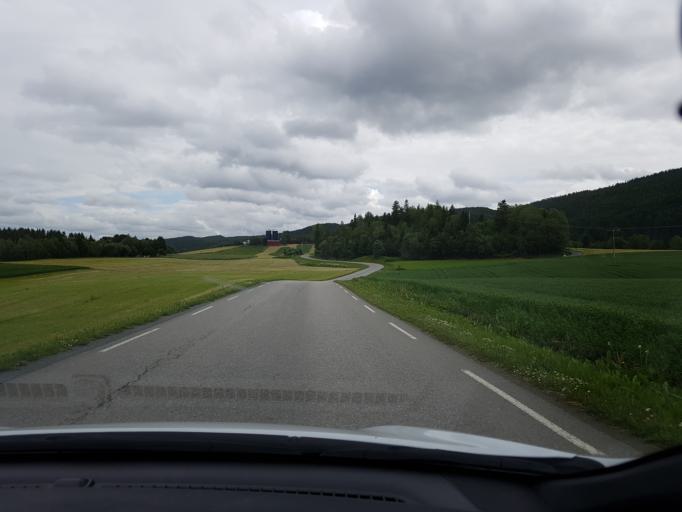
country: NO
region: Nord-Trondelag
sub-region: Levanger
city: Skogn
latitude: 63.6071
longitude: 11.0873
